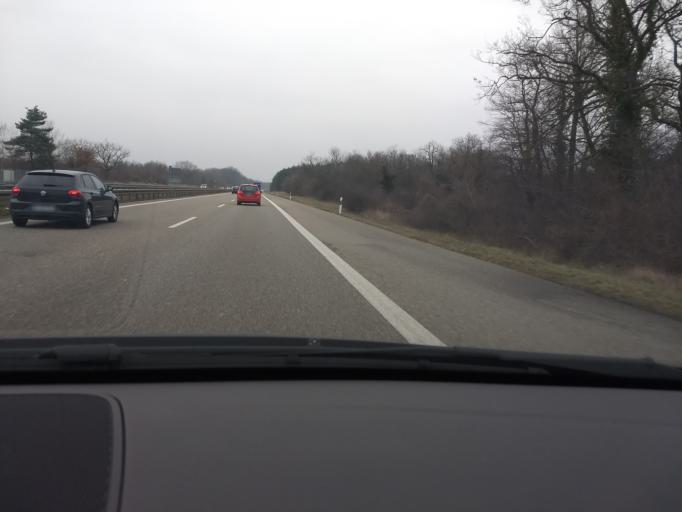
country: DE
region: Baden-Wuerttemberg
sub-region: Freiburg Region
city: Bad Bellingen
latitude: 47.7507
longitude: 7.5480
